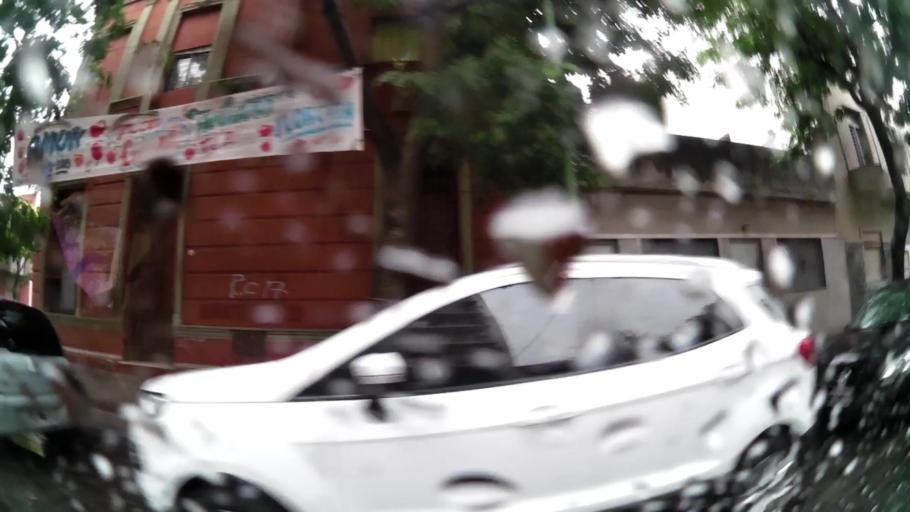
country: AR
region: Buenos Aires
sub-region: Partido de Avellaneda
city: Avellaneda
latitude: -34.6467
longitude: -58.3708
